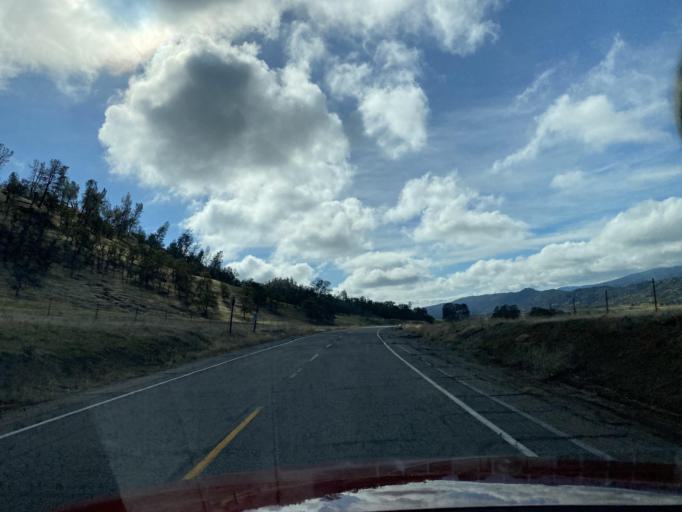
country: US
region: California
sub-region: Glenn County
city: Willows
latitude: 39.5689
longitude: -122.5401
